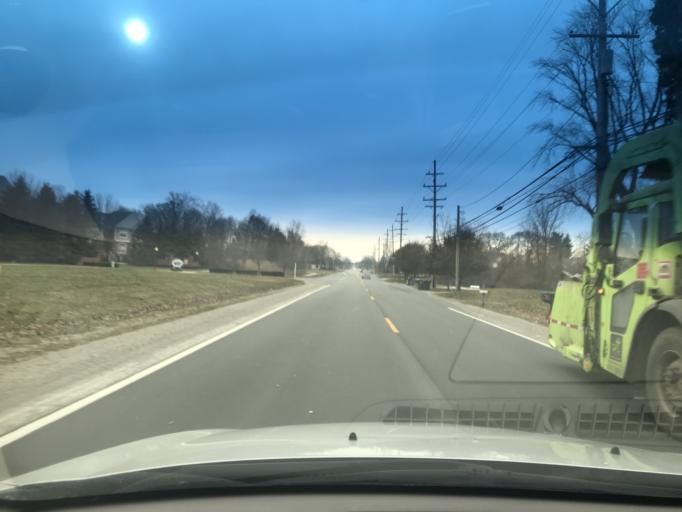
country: US
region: Michigan
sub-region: Macomb County
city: Shelby
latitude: 42.7029
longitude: -83.0547
